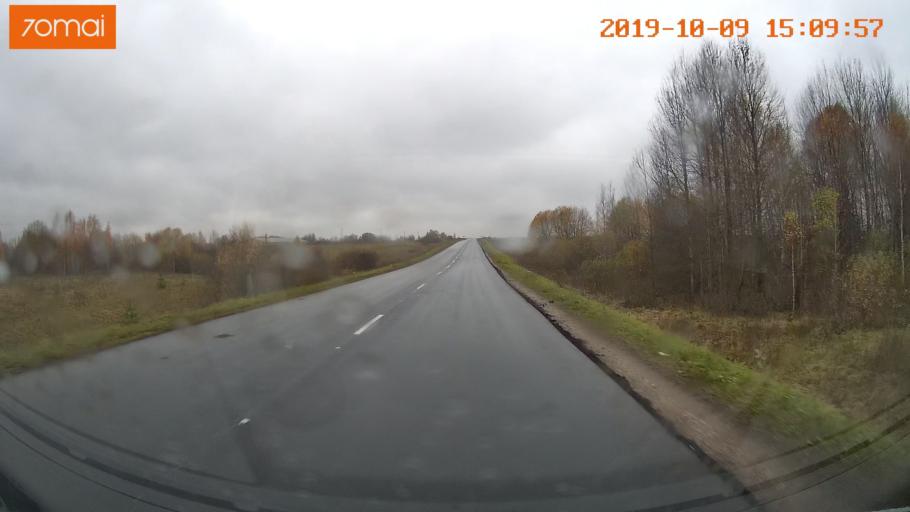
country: RU
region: Kostroma
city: Susanino
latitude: 58.1843
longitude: 41.6469
